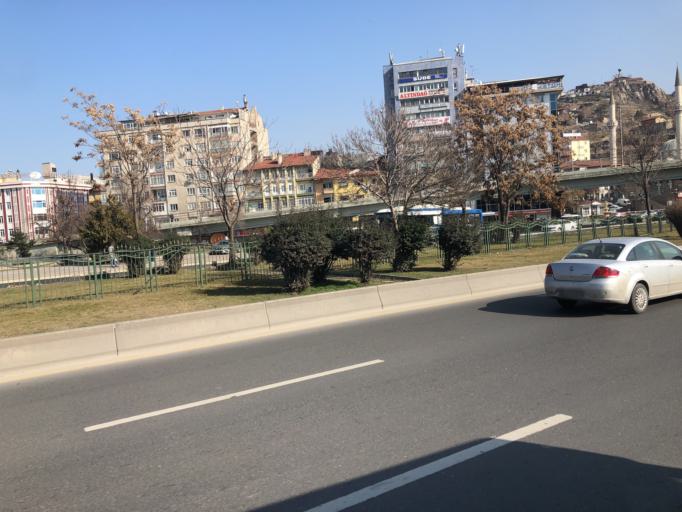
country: TR
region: Ankara
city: Ankara
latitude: 39.9518
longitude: 32.8576
